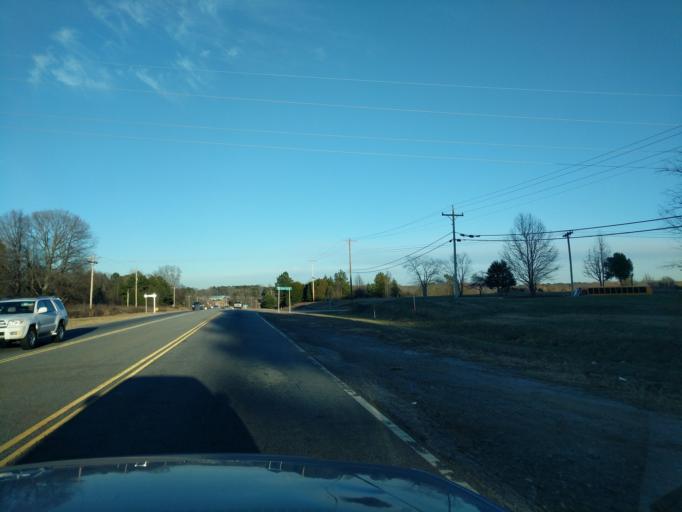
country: US
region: South Carolina
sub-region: Greenville County
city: Fountain Inn
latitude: 34.6770
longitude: -82.2093
